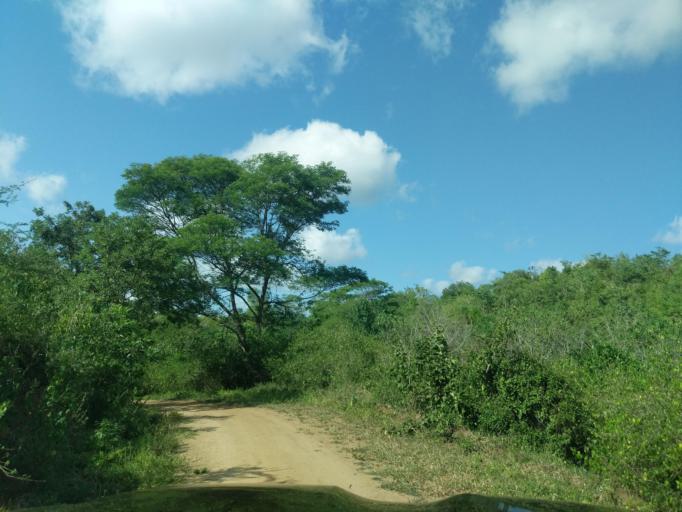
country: TZ
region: Tanga
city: Muheza
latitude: -5.4218
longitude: 38.6475
